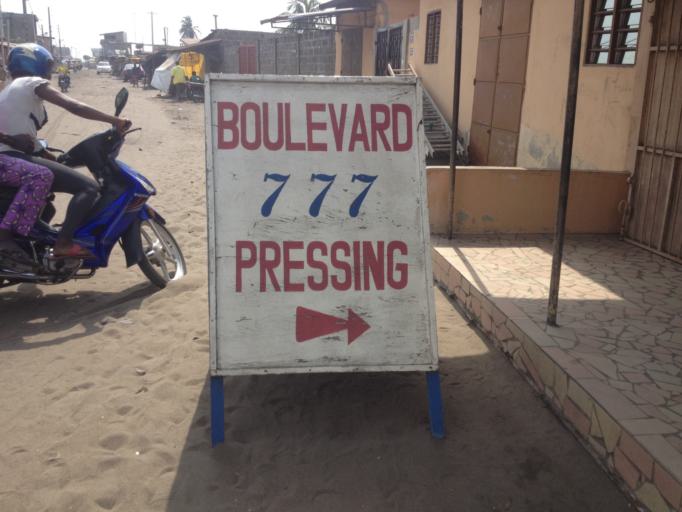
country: BJ
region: Littoral
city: Cotonou
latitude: 6.3579
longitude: 2.4470
